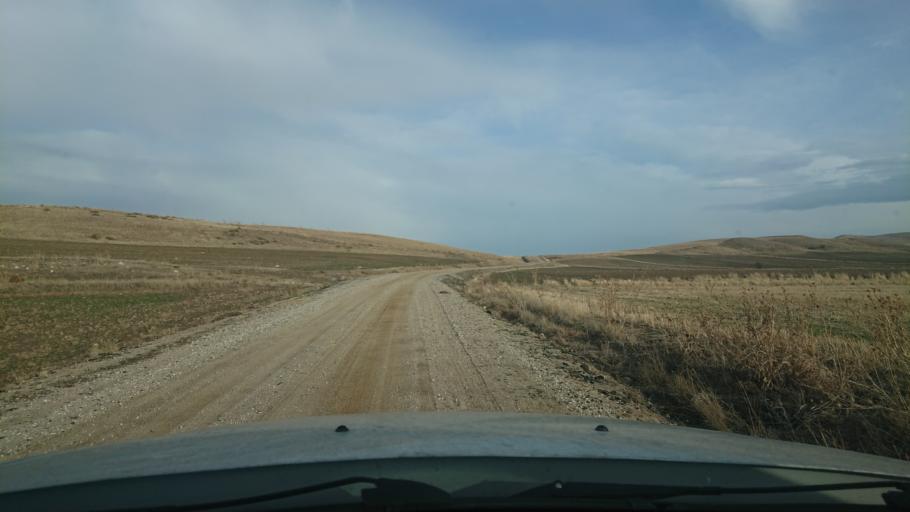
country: TR
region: Aksaray
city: Acipinar
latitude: 38.6854
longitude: 33.8697
